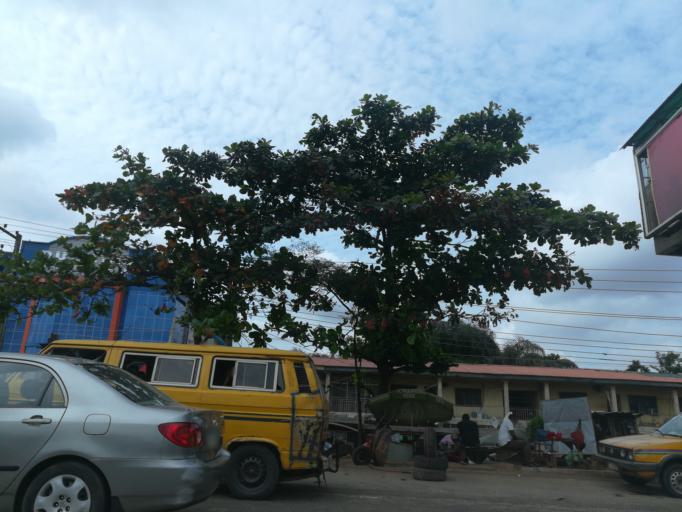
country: NG
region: Lagos
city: Somolu
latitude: 6.5483
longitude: 3.3794
